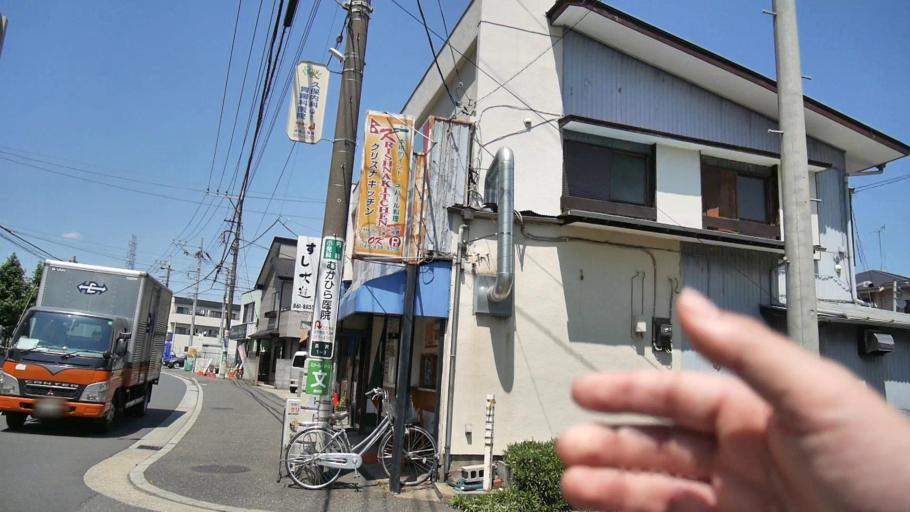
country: JP
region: Kanagawa
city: Fujisawa
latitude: 35.4020
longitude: 139.5205
